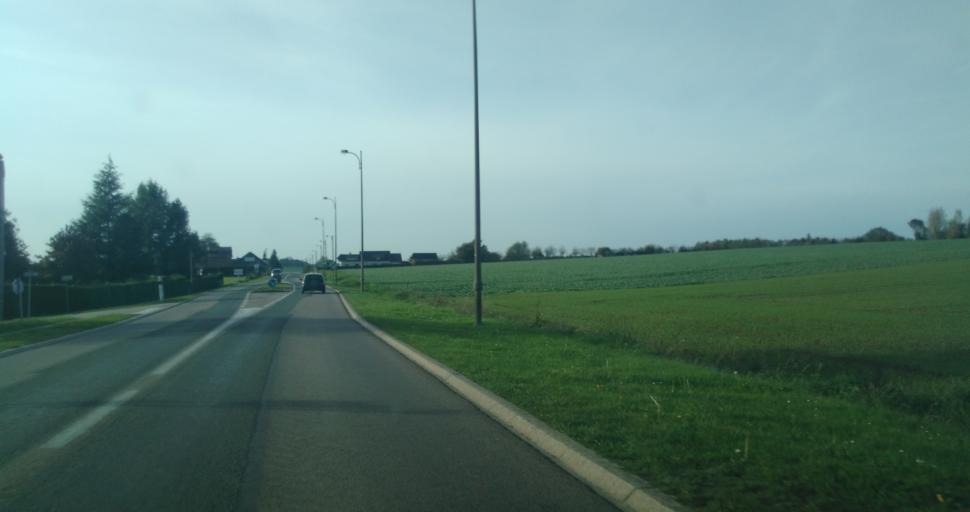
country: FR
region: Haute-Normandie
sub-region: Departement de l'Eure
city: Bourg-Achard
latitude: 49.3553
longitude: 0.8010
